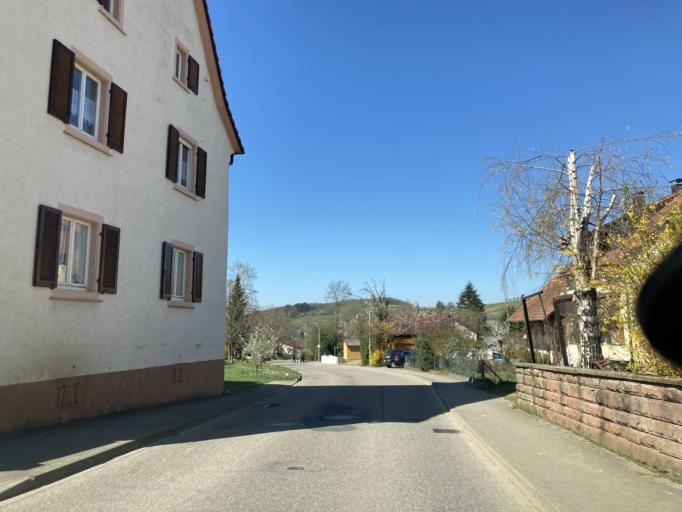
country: DE
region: Baden-Wuerttemberg
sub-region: Freiburg Region
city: Feldberg
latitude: 47.7568
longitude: 7.6448
